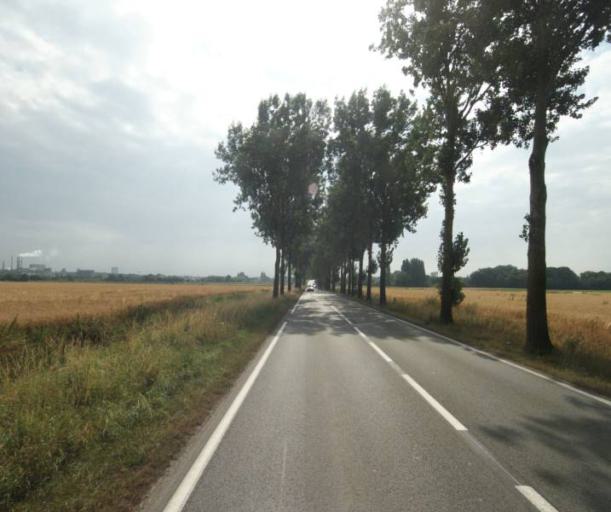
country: FR
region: Nord-Pas-de-Calais
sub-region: Departement du Nord
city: Santes
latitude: 50.6019
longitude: 2.9682
